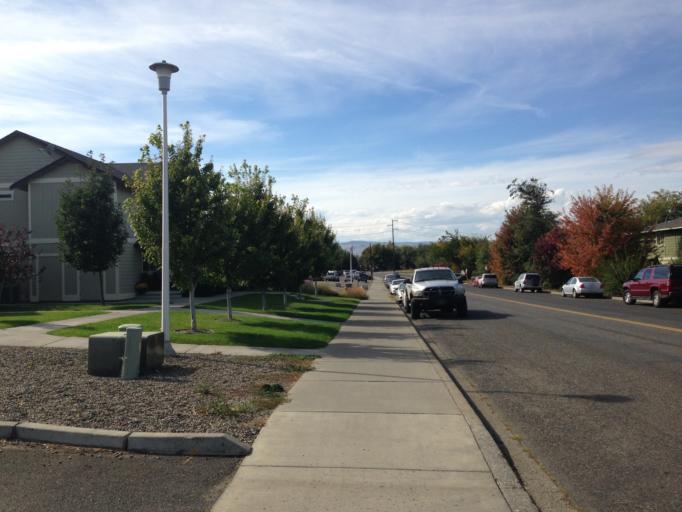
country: US
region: Washington
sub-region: Kittitas County
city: Ellensburg
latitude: 47.0060
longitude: -120.5454
